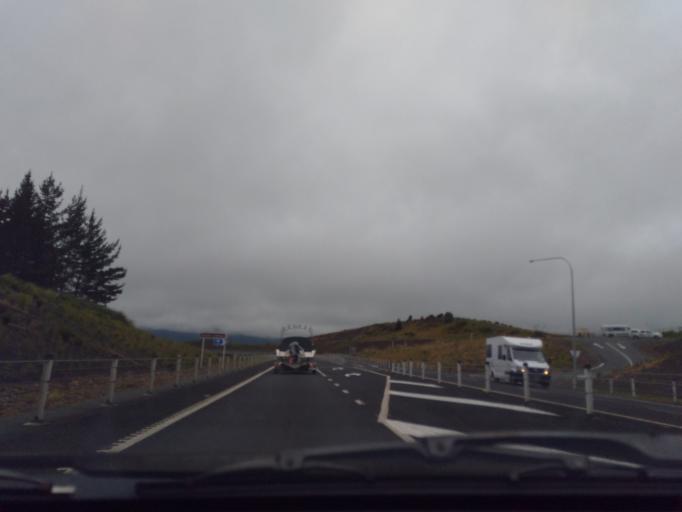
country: NZ
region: Northland
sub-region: Whangarei
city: Ruakaka
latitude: -36.0557
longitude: 174.4255
